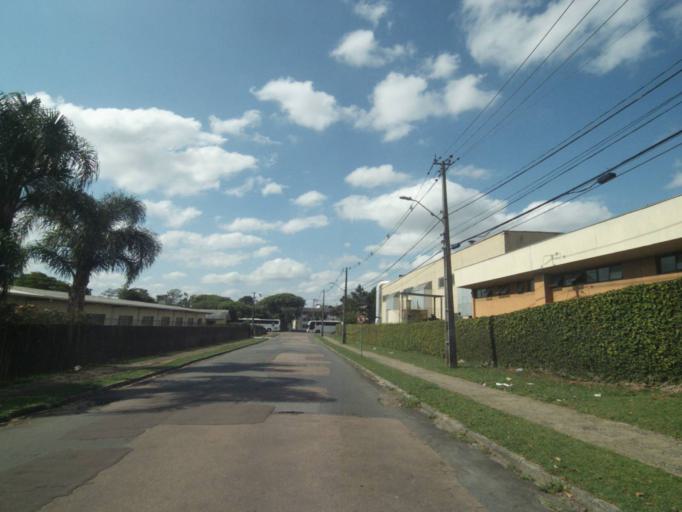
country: BR
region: Parana
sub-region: Curitiba
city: Curitiba
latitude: -25.4964
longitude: -49.3129
